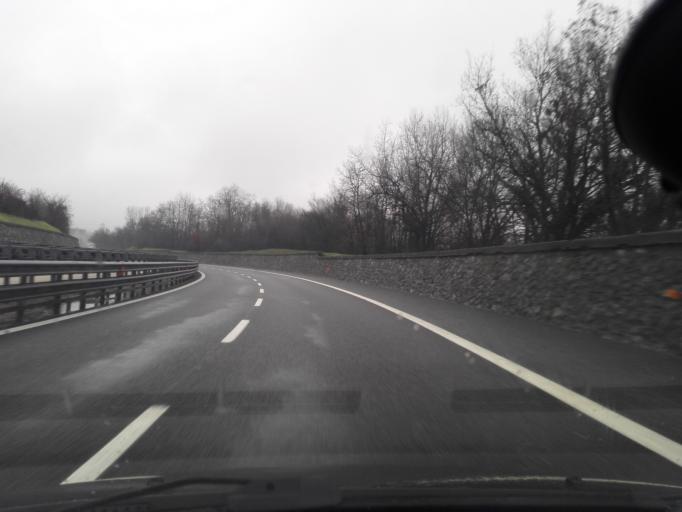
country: IT
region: Piedmont
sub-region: Provincia di Alessandria
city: Stazzano
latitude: 44.7111
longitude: 8.8699
